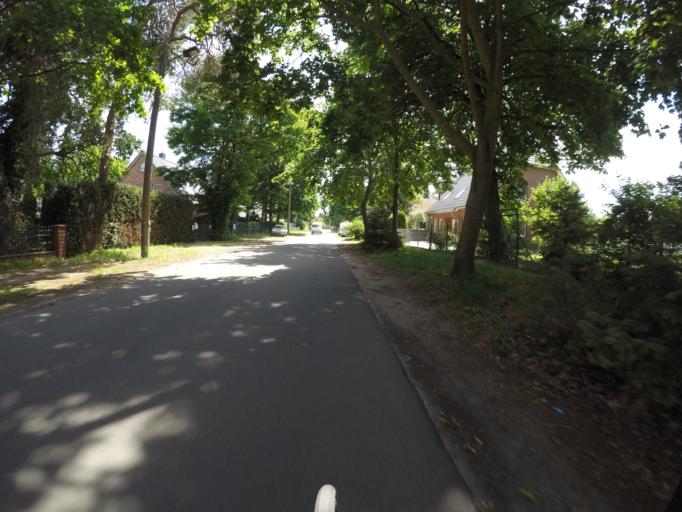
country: DE
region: Berlin
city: Mahlsdorf
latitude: 52.4921
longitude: 13.6191
